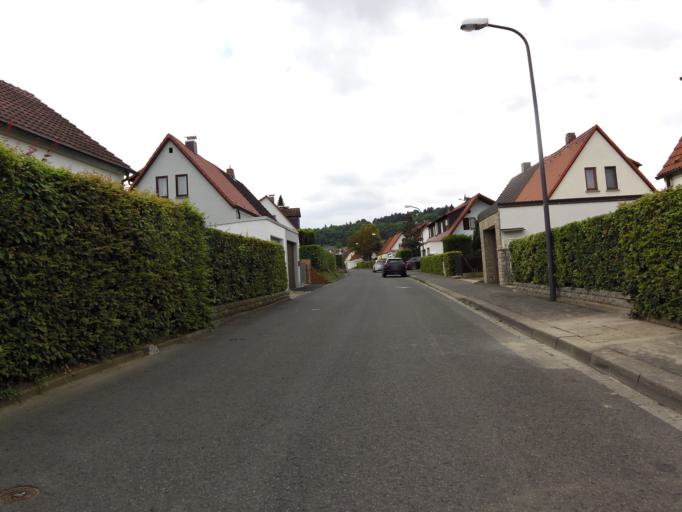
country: DE
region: Bavaria
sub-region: Regierungsbezirk Unterfranken
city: Wuerzburg
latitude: 49.7609
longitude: 9.9367
